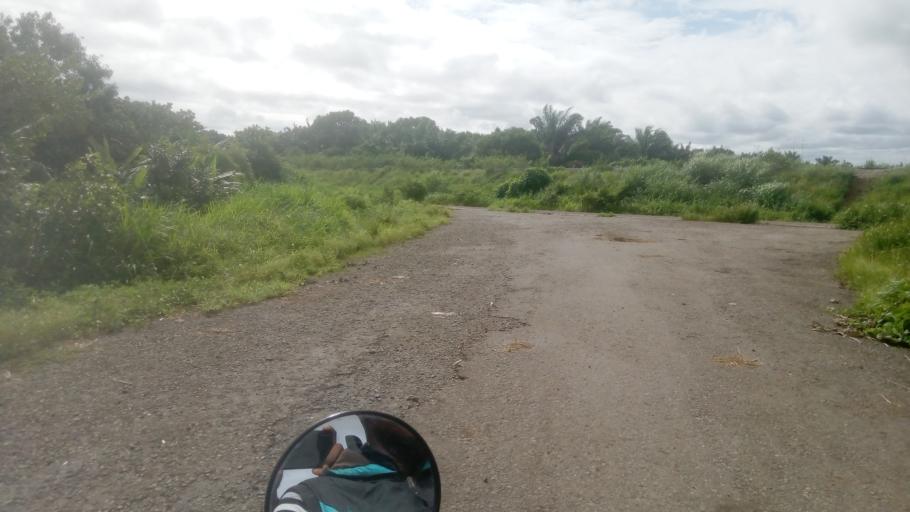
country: SL
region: Northern Province
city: Port Loko
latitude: 8.7098
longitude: -12.6764
